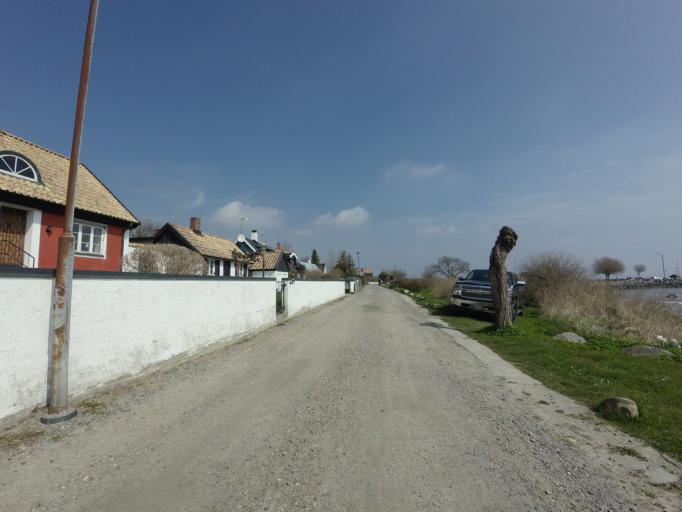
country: SE
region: Skane
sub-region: Skurups Kommun
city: Skivarp
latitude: 55.3931
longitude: 13.6004
